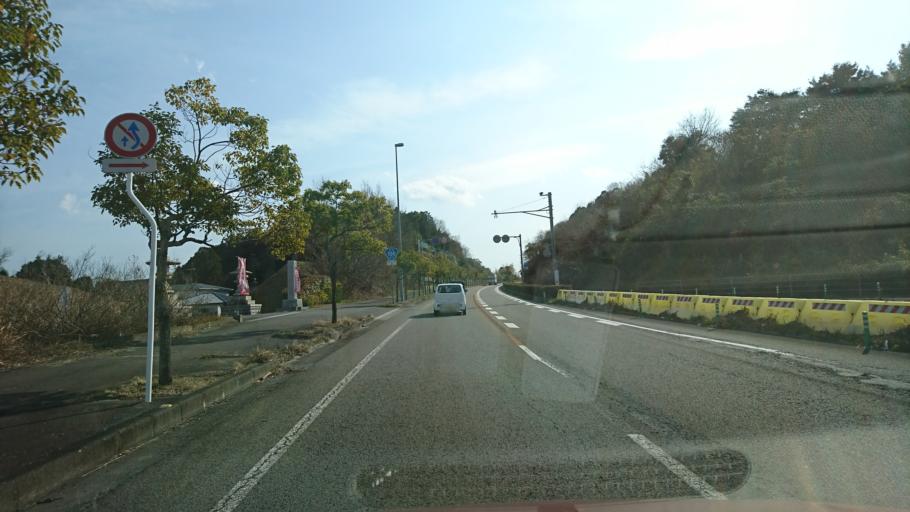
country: JP
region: Ehime
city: Saijo
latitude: 34.0164
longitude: 133.0320
